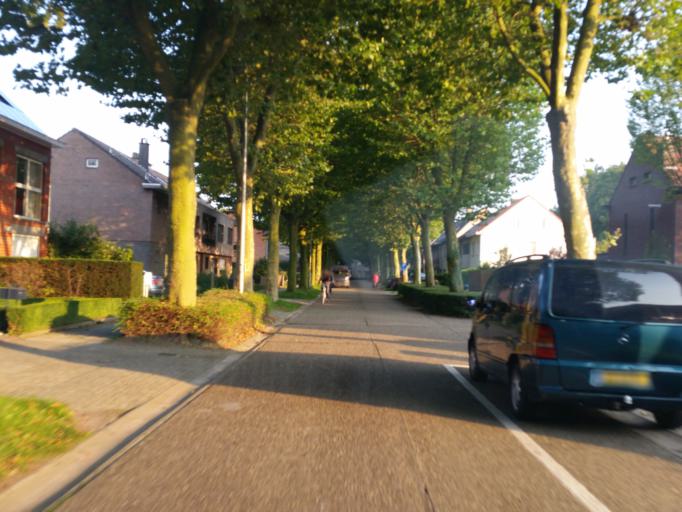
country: BE
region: Flanders
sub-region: Provincie Antwerpen
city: Brasschaat
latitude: 51.2960
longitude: 4.5048
